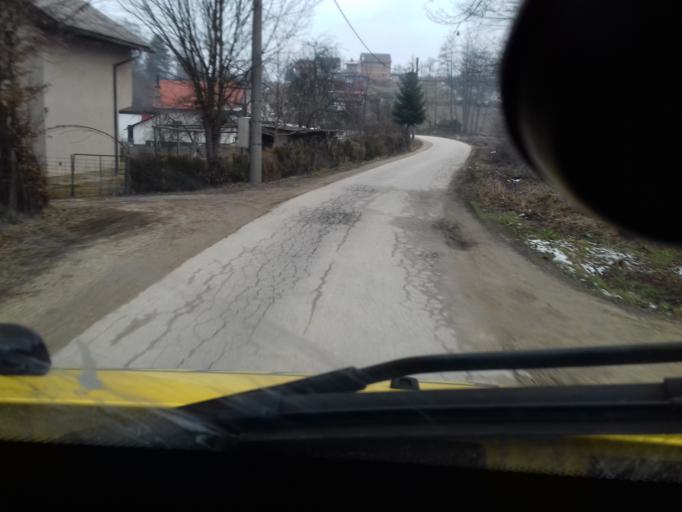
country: BA
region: Federation of Bosnia and Herzegovina
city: Busovaca
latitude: 44.1160
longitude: 17.8504
